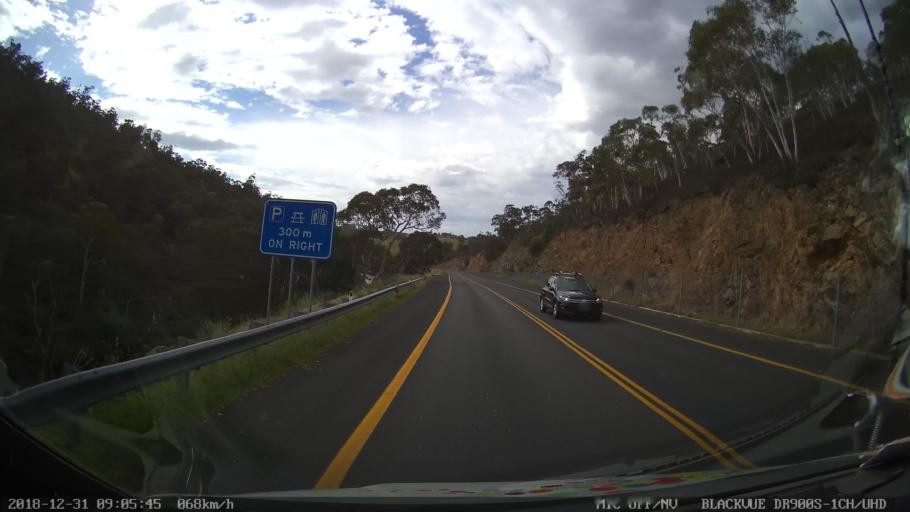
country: AU
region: New South Wales
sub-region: Snowy River
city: Jindabyne
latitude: -36.3664
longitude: 148.5878
